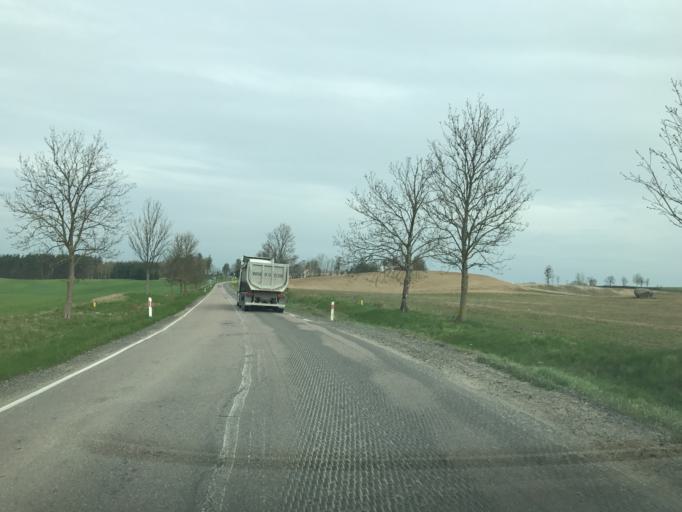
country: PL
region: Warmian-Masurian Voivodeship
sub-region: Powiat ostrodzki
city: Gierzwald
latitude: 53.5783
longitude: 20.0918
